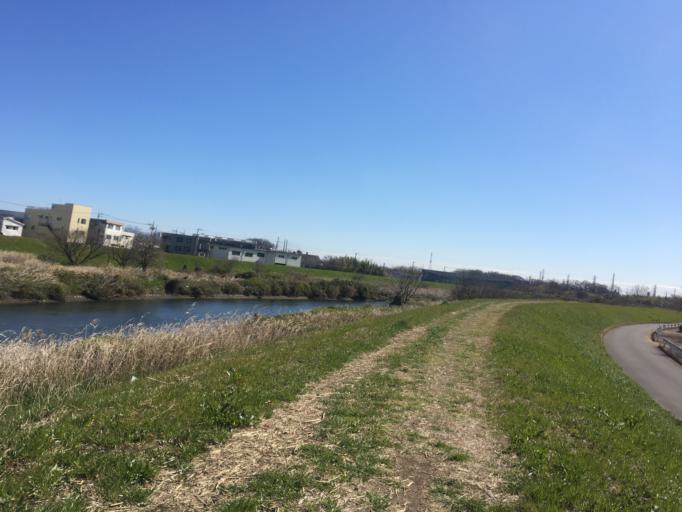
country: JP
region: Saitama
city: Asaka
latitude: 35.8195
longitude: 139.6073
